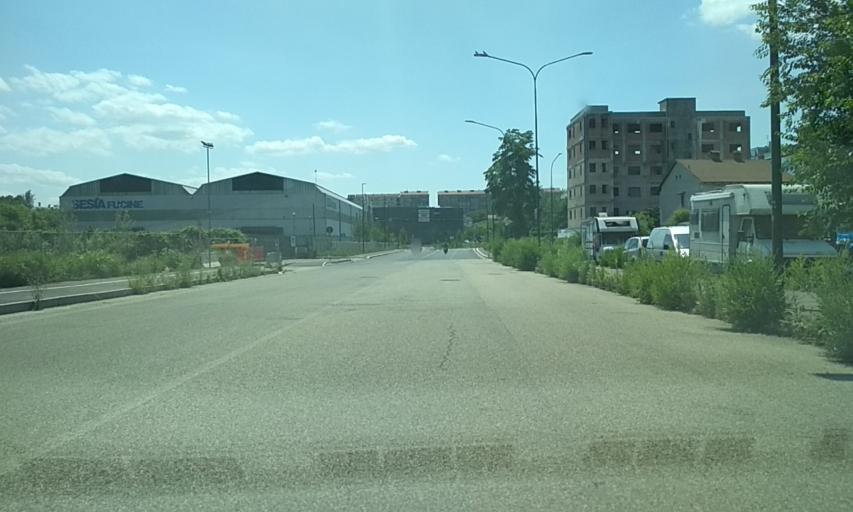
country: IT
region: Piedmont
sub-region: Provincia di Torino
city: Turin
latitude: 45.1052
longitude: 7.7070
